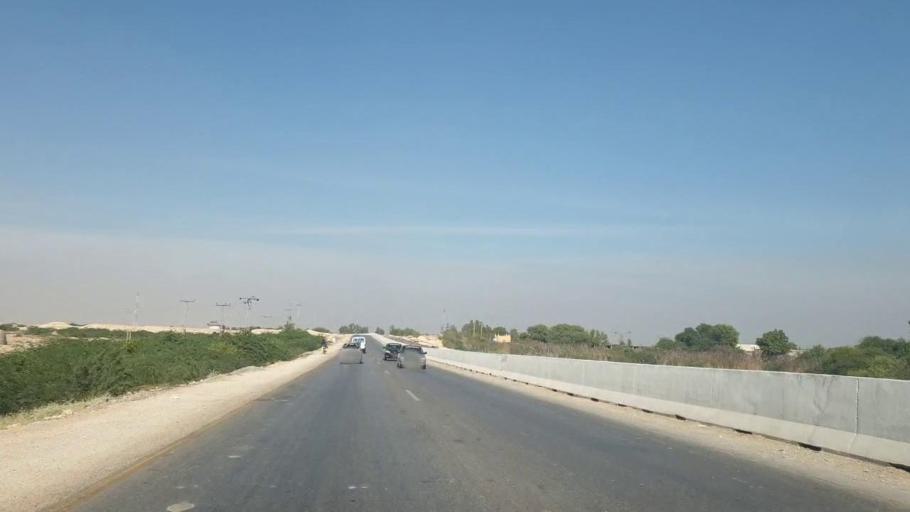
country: PK
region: Sindh
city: Hala
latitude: 25.7089
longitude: 68.2958
